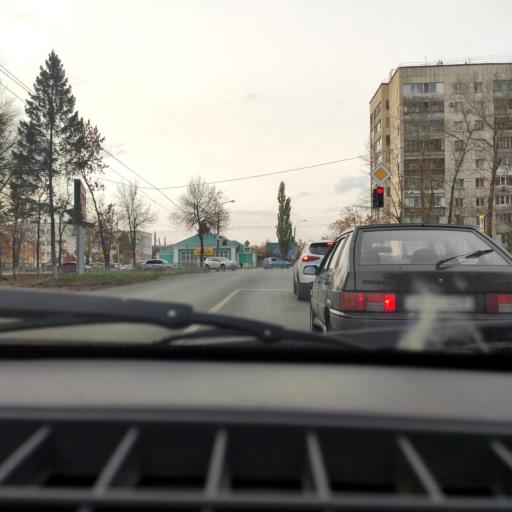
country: RU
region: Bashkortostan
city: Avdon
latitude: 54.6967
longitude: 55.8260
